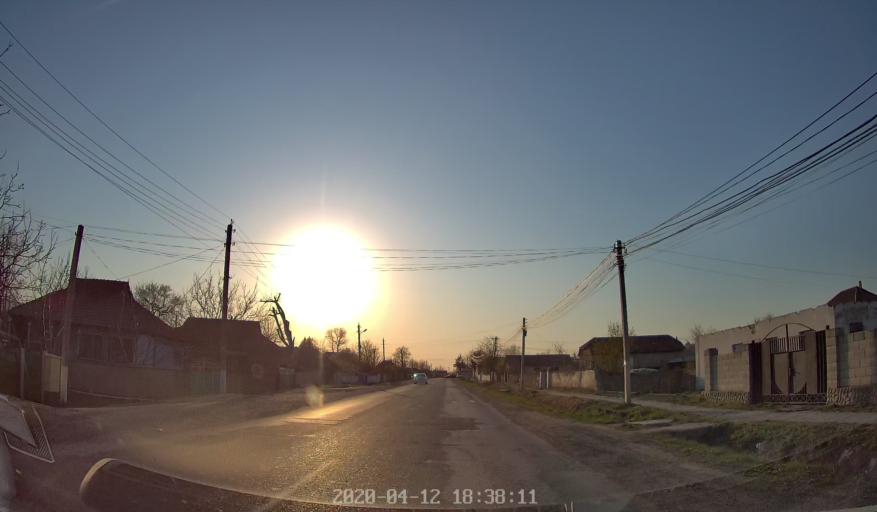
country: MD
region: Chisinau
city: Vadul lui Voda
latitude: 47.1236
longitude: 29.0042
